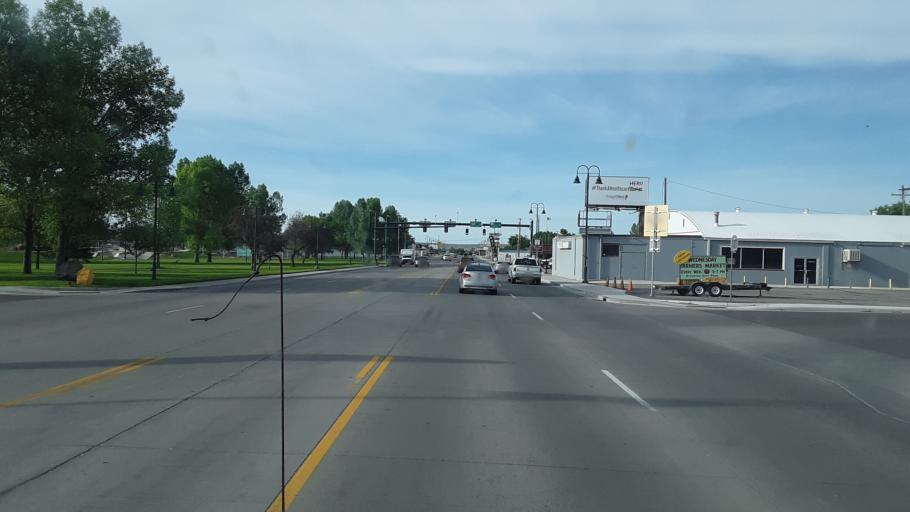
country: US
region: Wyoming
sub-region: Fremont County
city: Riverton
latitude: 43.0260
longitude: -108.3807
